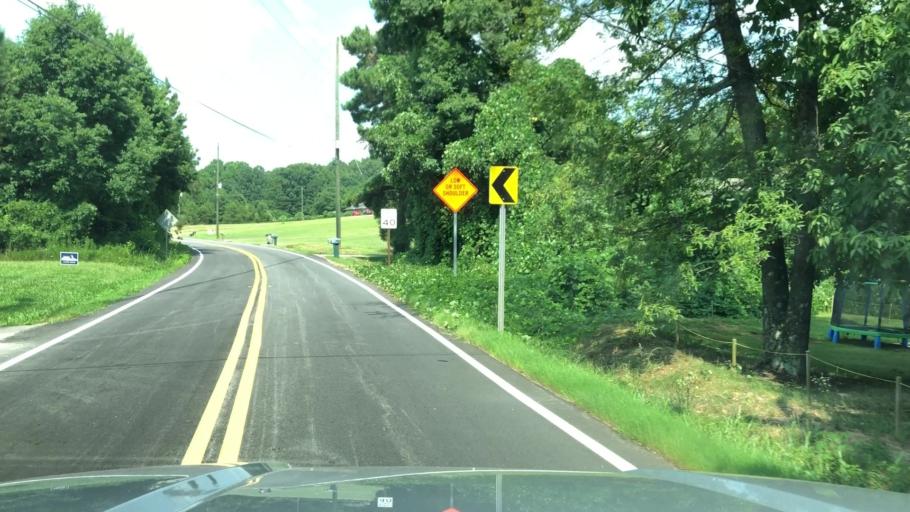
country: US
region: Georgia
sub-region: Paulding County
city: Hiram
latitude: 33.9425
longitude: -84.7368
